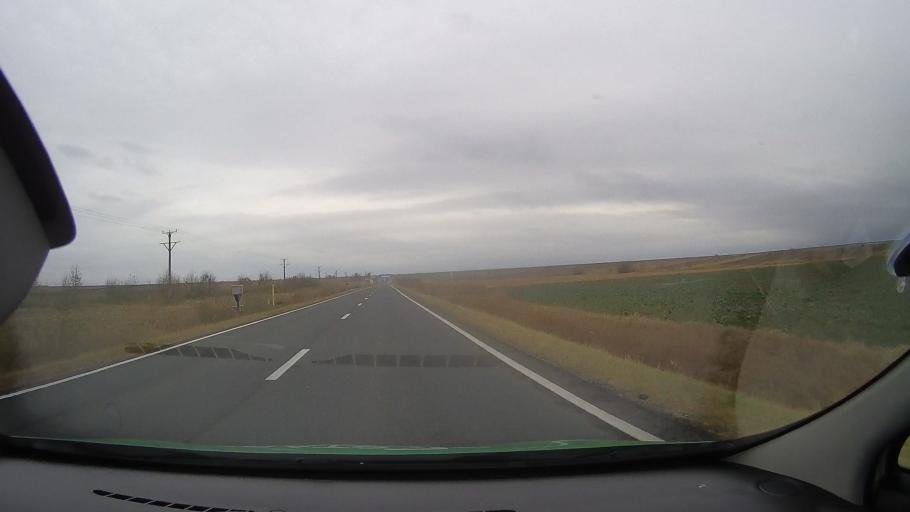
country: RO
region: Constanta
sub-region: Comuna Nicolae Balcescu
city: Nicolae Balcescu
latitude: 44.3849
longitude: 28.3940
